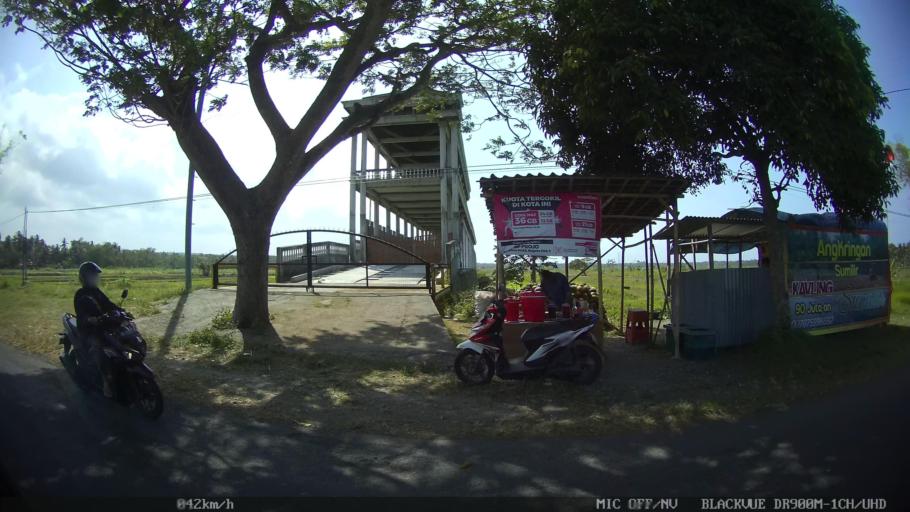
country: ID
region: Daerah Istimewa Yogyakarta
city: Srandakan
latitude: -7.8987
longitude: 110.1526
